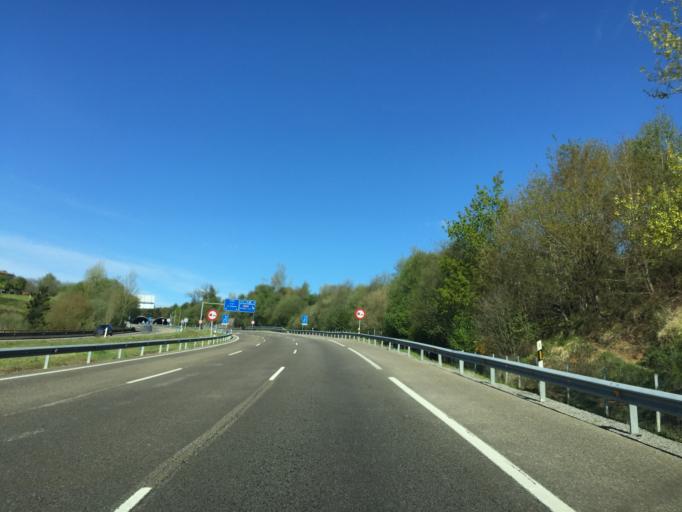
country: ES
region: Asturias
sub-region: Province of Asturias
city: Oviedo
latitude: 43.3431
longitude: -5.8853
